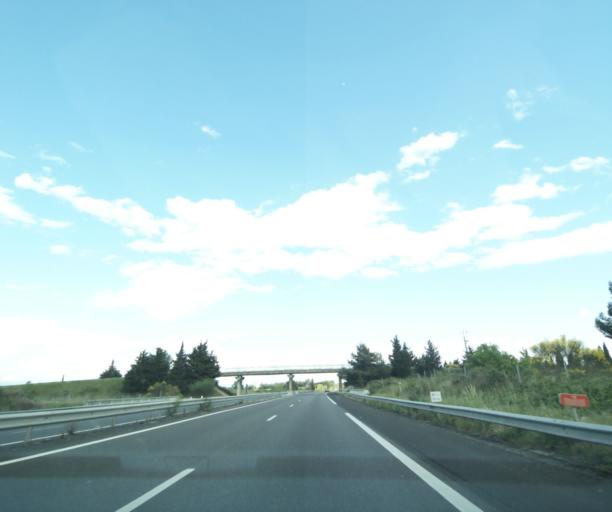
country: FR
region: Languedoc-Roussillon
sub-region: Departement du Gard
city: Garons
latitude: 43.7412
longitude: 4.4517
